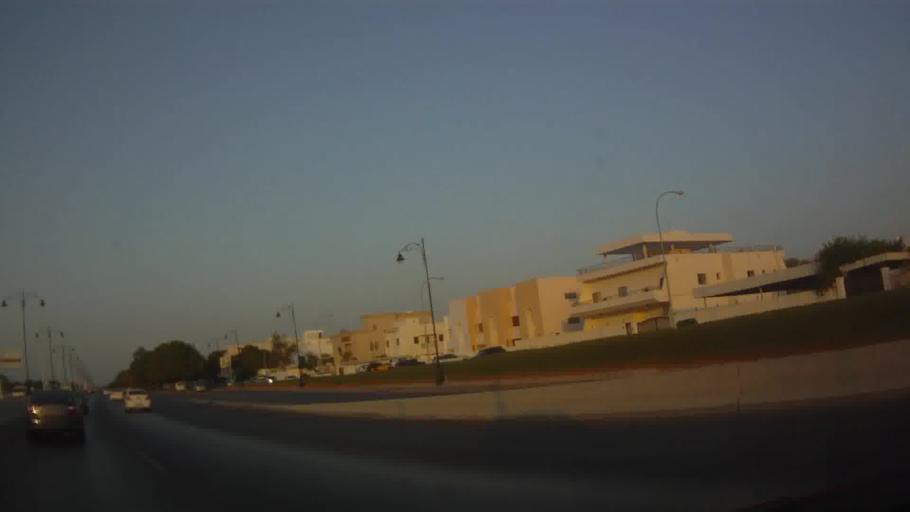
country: OM
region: Muhafazat Masqat
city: Bawshar
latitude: 23.5999
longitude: 58.4457
